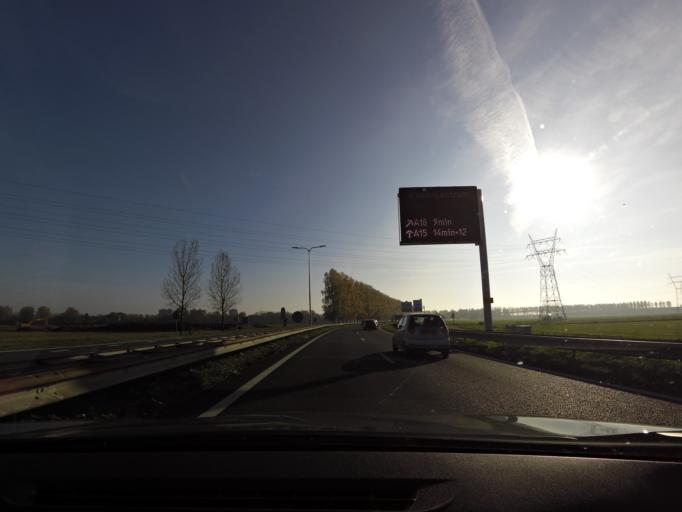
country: NL
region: South Holland
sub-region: Gemeente Ridderkerk
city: Ridderkerk
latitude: 51.8841
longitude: 4.5802
